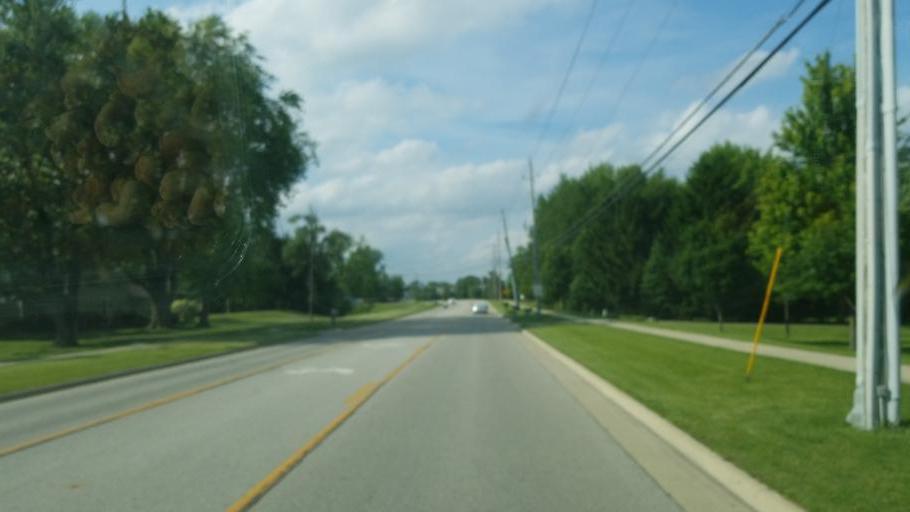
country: US
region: Ohio
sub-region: Franklin County
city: Westerville
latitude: 40.1657
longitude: -82.8996
